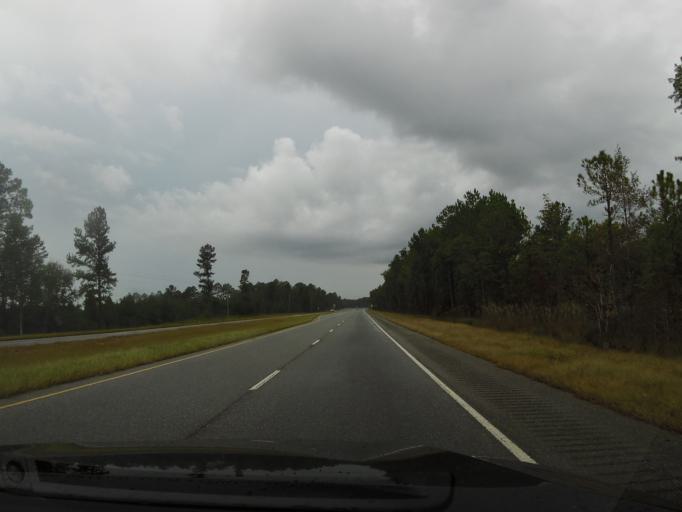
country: US
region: Georgia
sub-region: Wayne County
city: Jesup
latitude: 31.5465
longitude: -81.8080
